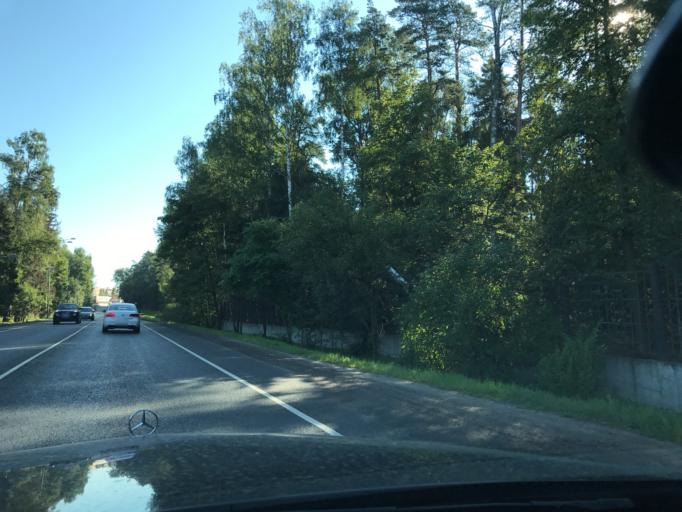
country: RU
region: Moskovskaya
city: Sverdlovskiy
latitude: 55.9172
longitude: 38.1200
